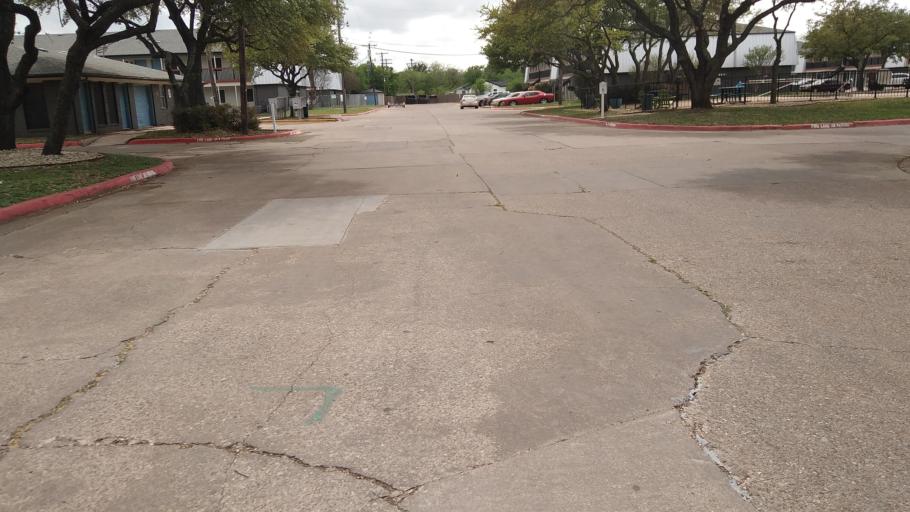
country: US
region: Texas
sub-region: McLennan County
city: Beverly
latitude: 31.5244
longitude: -97.1237
